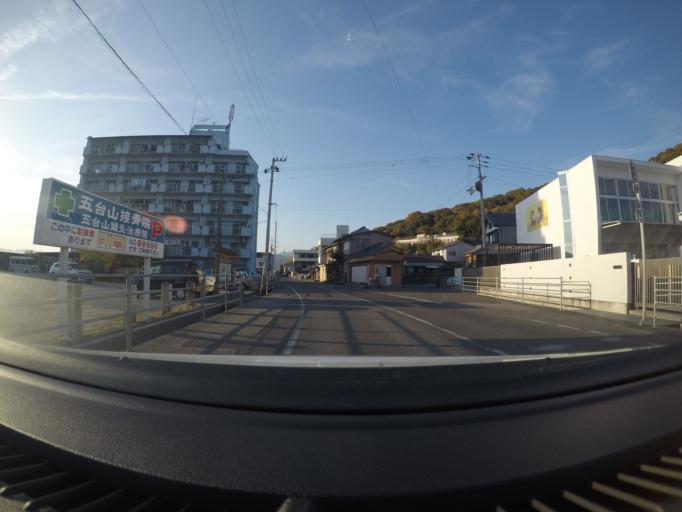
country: JP
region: Kochi
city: Kochi-shi
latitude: 33.5460
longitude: 133.5701
